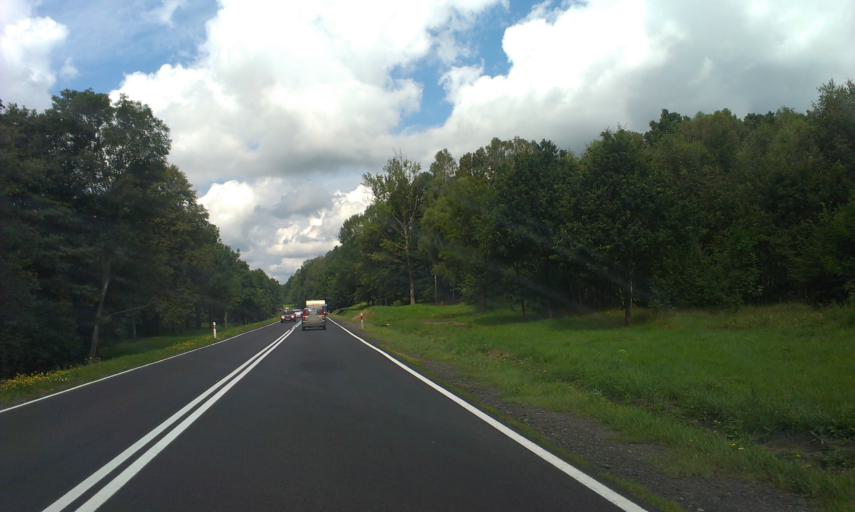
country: PL
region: West Pomeranian Voivodeship
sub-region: Powiat koszalinski
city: Bobolice
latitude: 53.9694
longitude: 16.5615
